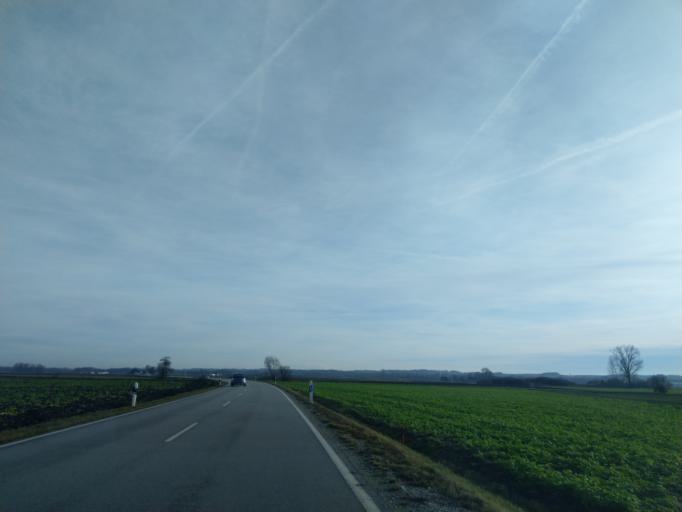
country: DE
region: Bavaria
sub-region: Lower Bavaria
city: Wallersdorf
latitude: 48.7257
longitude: 12.7810
